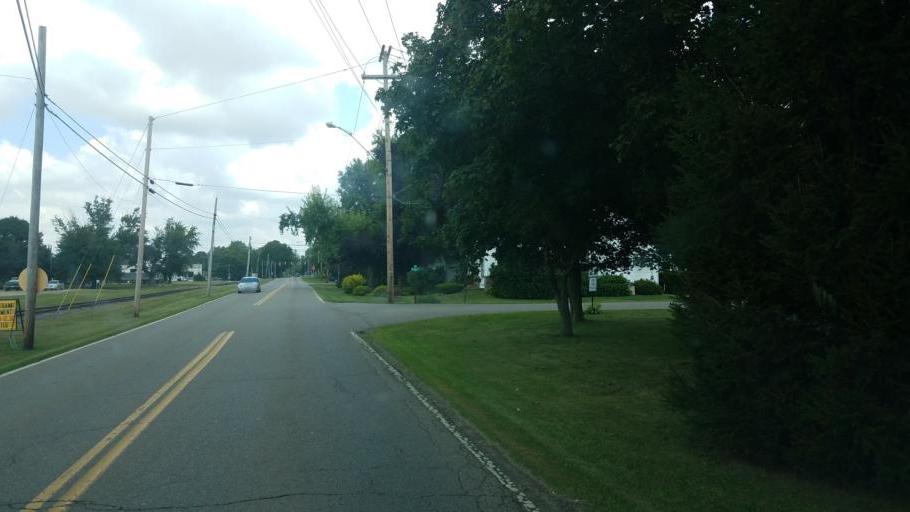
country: US
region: Ohio
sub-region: Knox County
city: Mount Vernon
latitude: 40.3727
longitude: -82.4877
